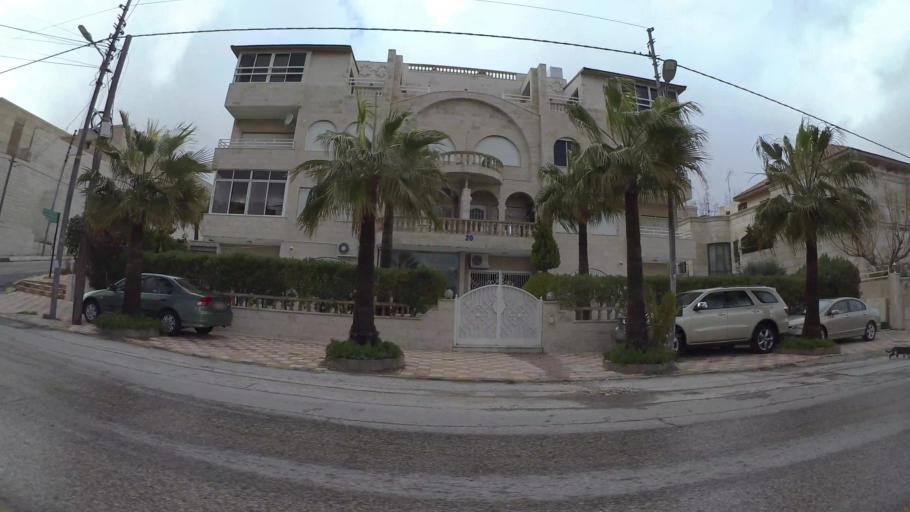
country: JO
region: Amman
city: Al Bunayyat ash Shamaliyah
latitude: 31.9465
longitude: 35.8885
